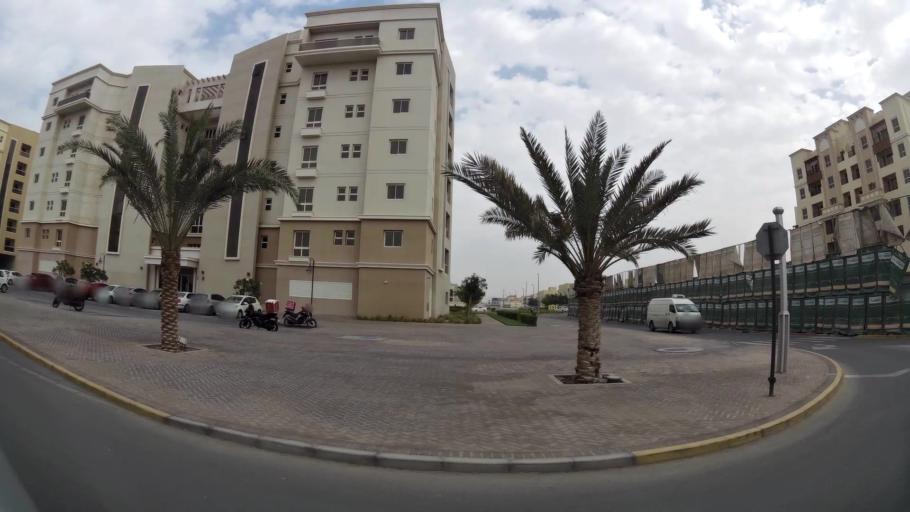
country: AE
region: Abu Dhabi
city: Abu Dhabi
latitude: 24.3136
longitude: 54.6215
